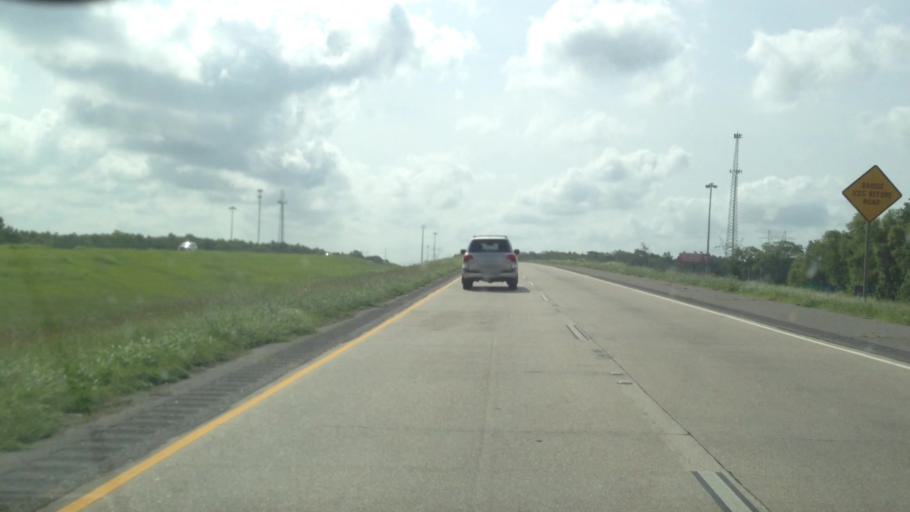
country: US
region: Louisiana
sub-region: Ascension Parish
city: Sorrento
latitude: 30.1728
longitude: -90.8801
